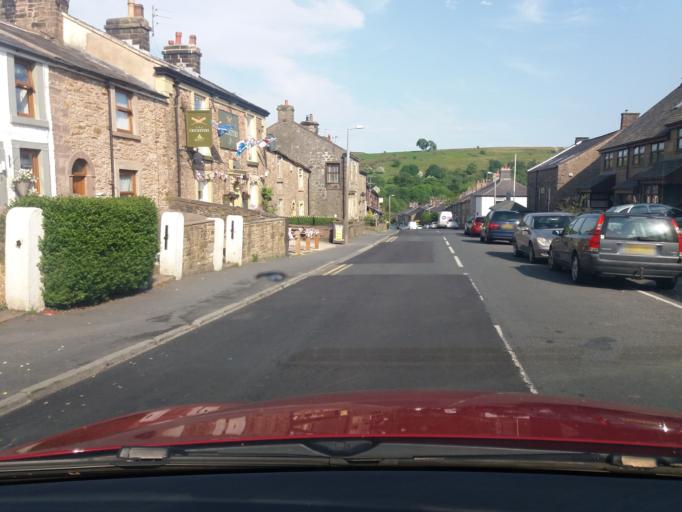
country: GB
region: England
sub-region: Lancashire
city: Chorley
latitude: 53.6884
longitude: -2.5697
